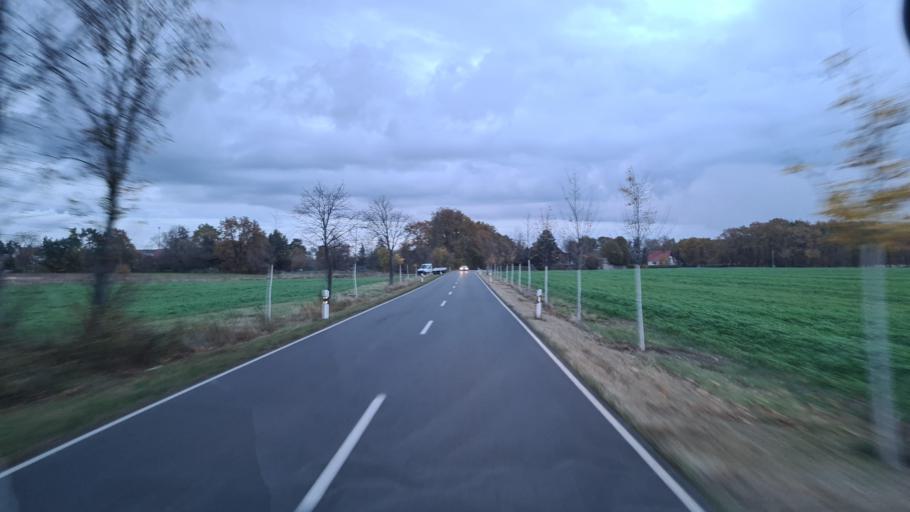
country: DE
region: Saxony-Anhalt
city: Holzdorf
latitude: 51.7763
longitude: 13.1082
